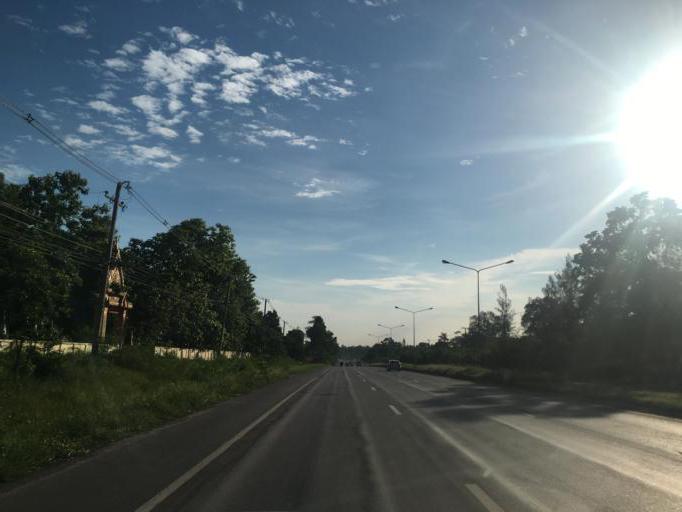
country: TH
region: Changwat Udon Thani
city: Kut Chap
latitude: 17.3308
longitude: 102.6556
